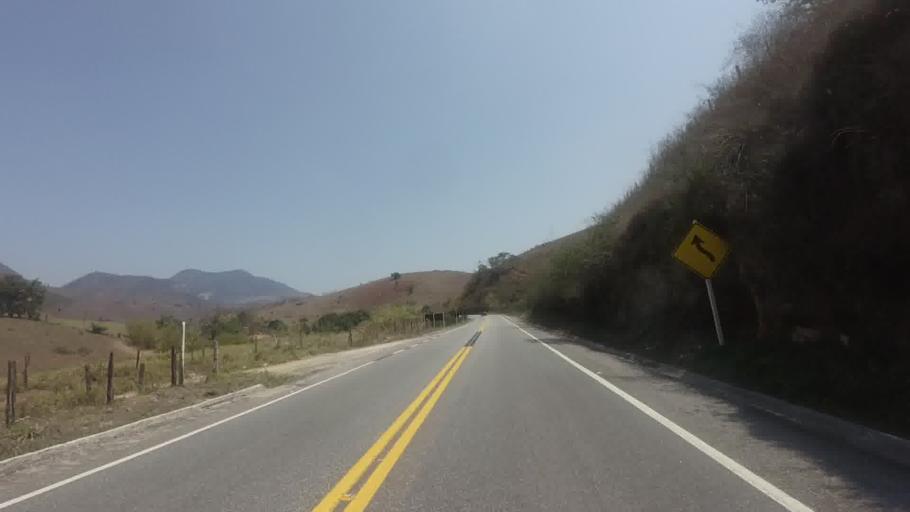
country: BR
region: Espirito Santo
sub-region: Mimoso Do Sul
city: Mimoso do Sul
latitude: -20.9213
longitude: -41.3100
